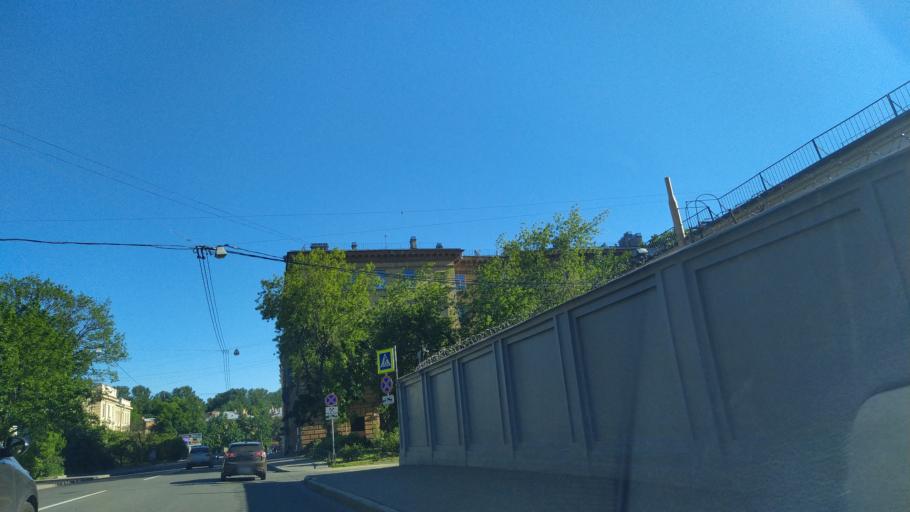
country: RU
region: Leningrad
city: Finlyandskiy
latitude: 59.9614
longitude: 30.3447
